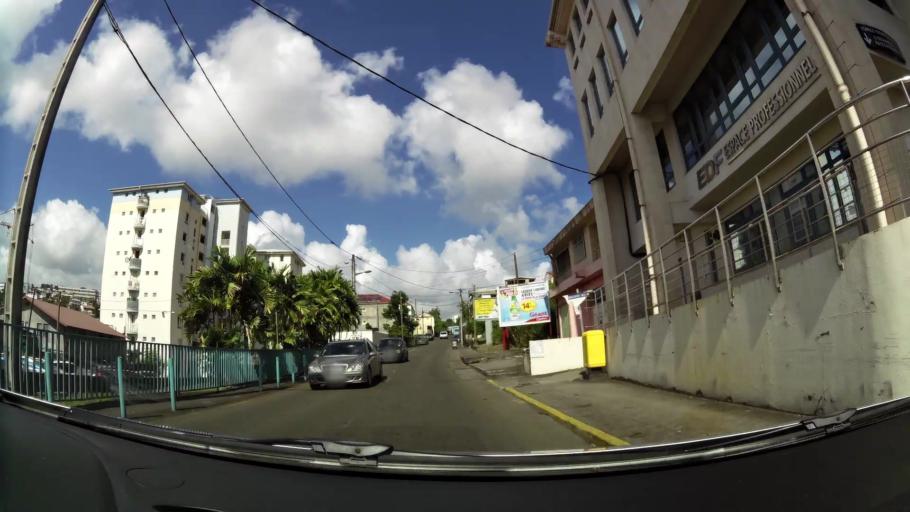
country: MQ
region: Martinique
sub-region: Martinique
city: Fort-de-France
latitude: 14.6052
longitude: -61.0632
